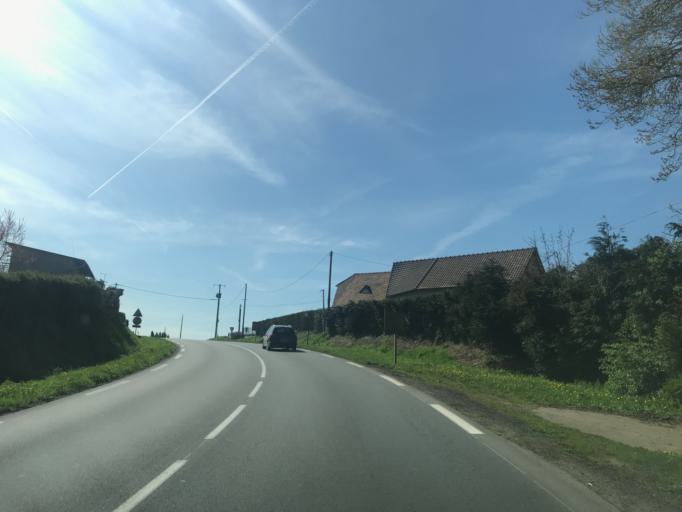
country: FR
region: Haute-Normandie
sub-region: Departement de l'Eure
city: Fleury-sur-Andelle
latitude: 49.3544
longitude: 1.3619
